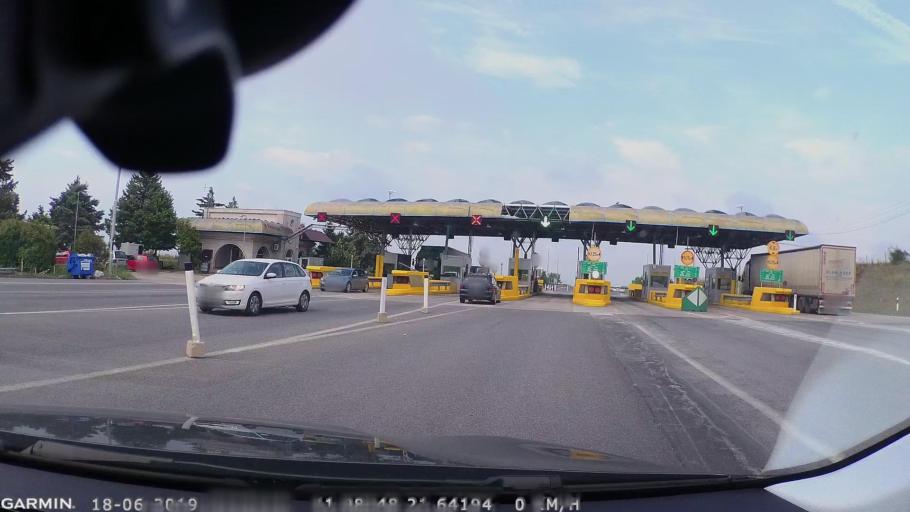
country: MK
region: Petrovec
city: Sredno Konjare
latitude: 41.9553
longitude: 21.7400
